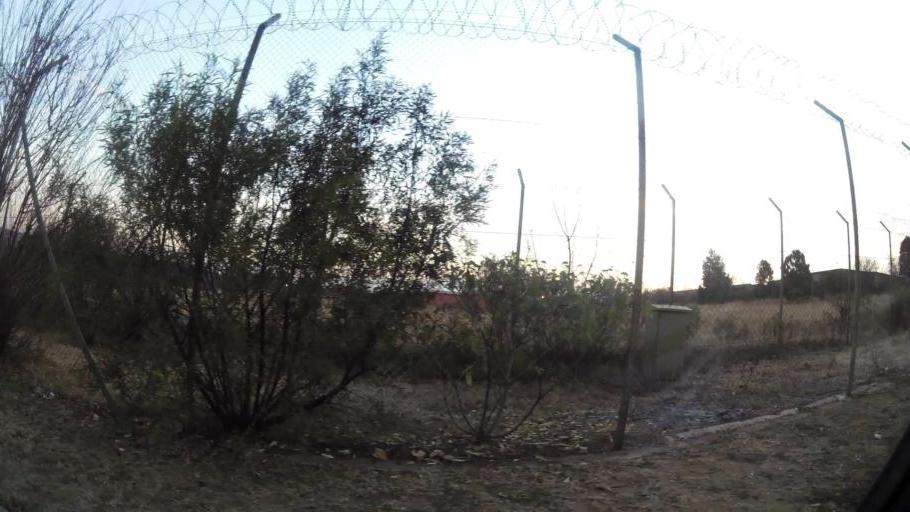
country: ZA
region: Gauteng
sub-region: City of Johannesburg Metropolitan Municipality
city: Midrand
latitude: -26.0069
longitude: 28.0488
